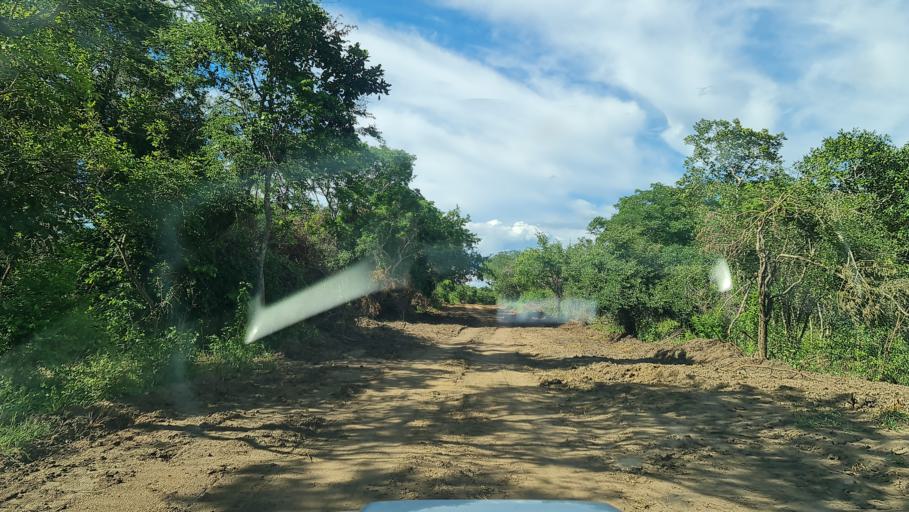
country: MZ
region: Nampula
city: Antonio Enes
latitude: -15.5157
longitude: 40.1303
